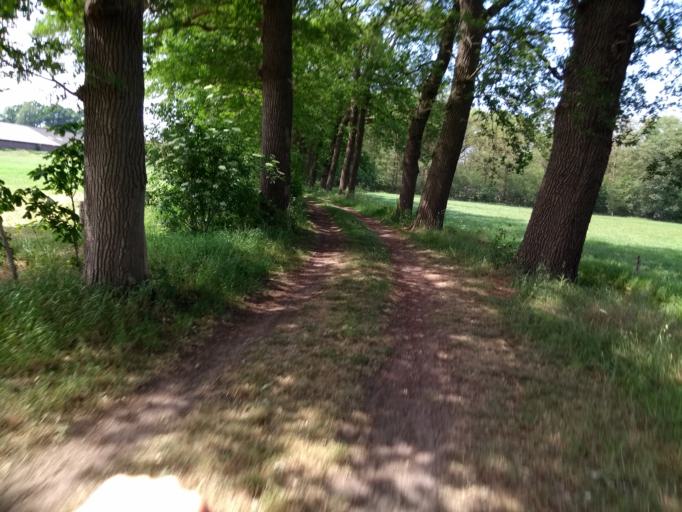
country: NL
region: Overijssel
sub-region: Gemeente Almelo
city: Almelo
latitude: 52.3606
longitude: 6.7066
